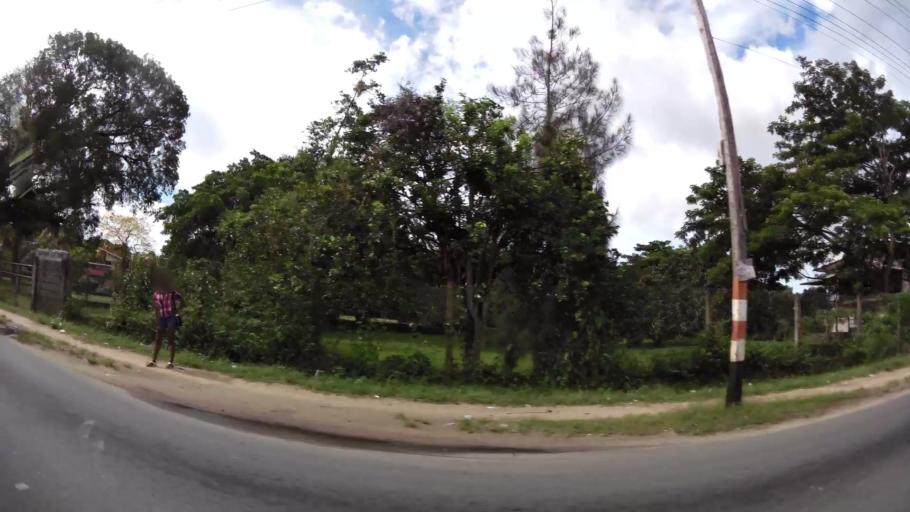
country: SR
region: Paramaribo
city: Paramaribo
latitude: 5.8410
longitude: -55.1885
